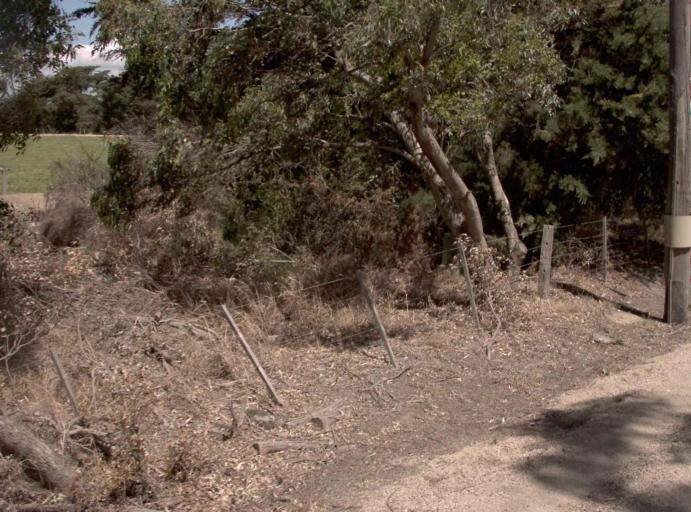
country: AU
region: Victoria
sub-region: Wellington
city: Heyfield
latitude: -38.0423
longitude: 146.8768
